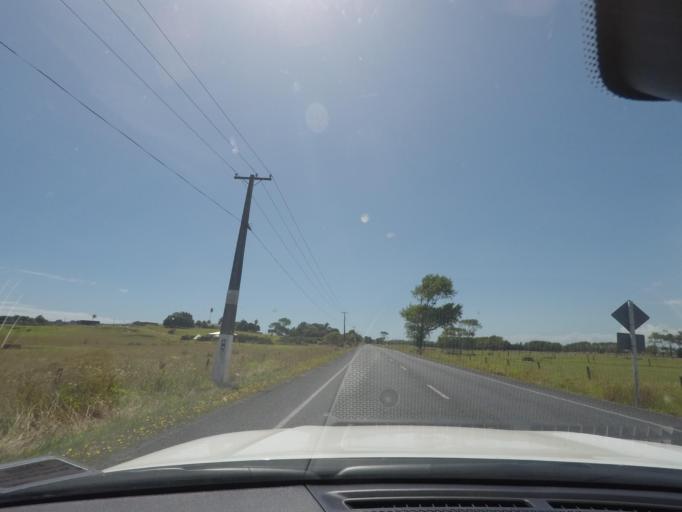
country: NZ
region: Auckland
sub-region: Auckland
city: Parakai
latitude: -36.7022
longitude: 174.4368
